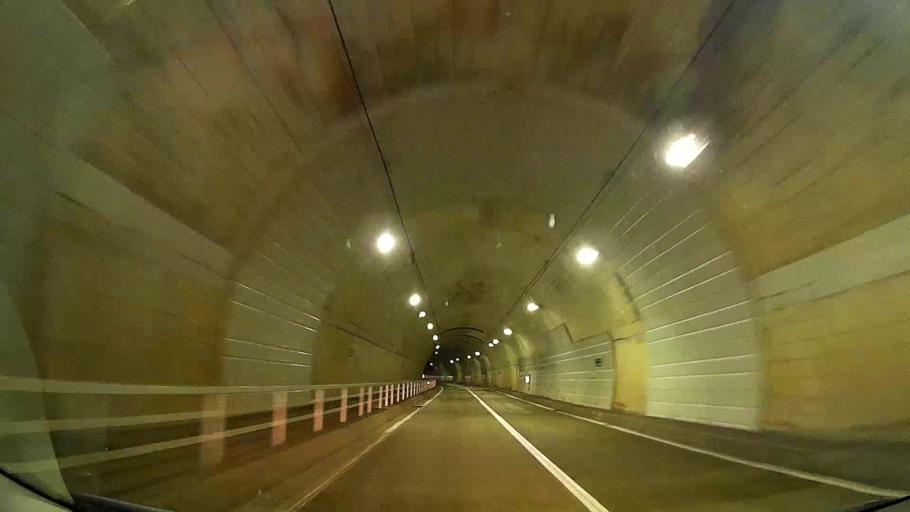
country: JP
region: Hokkaido
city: Sapporo
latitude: 42.9929
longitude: 141.1601
